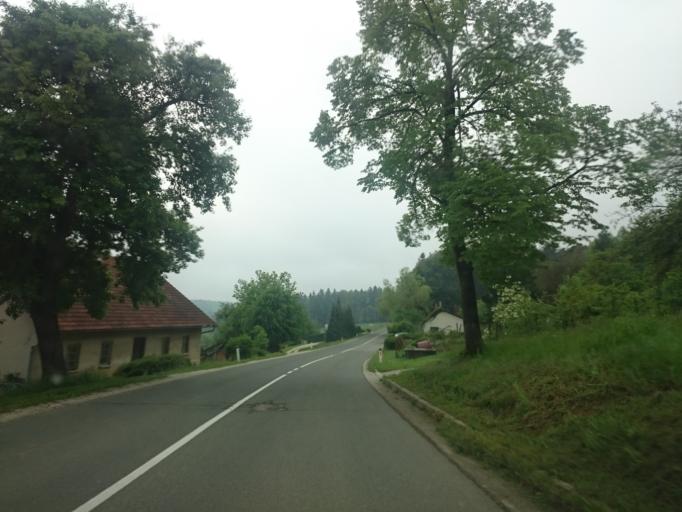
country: SI
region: Sentjur pri Celju
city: Sentjur
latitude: 46.2697
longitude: 15.3934
